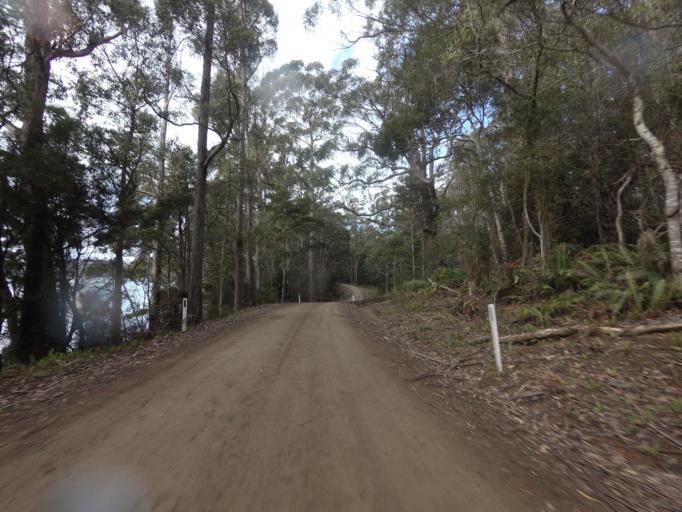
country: AU
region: Tasmania
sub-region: Huon Valley
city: Geeveston
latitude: -43.5682
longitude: 146.8890
